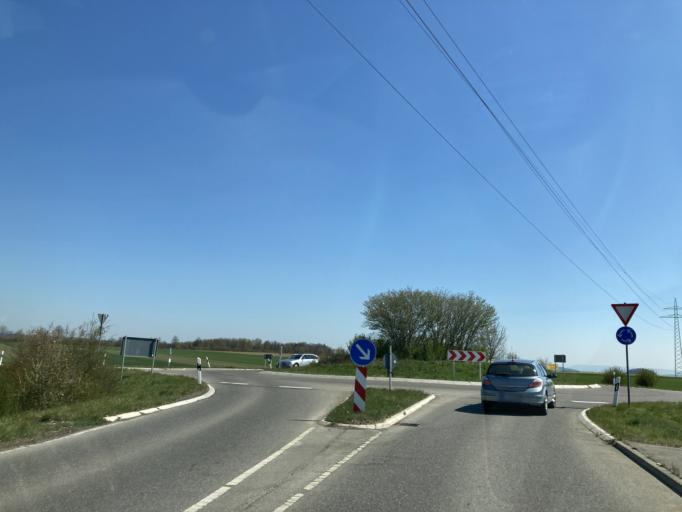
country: DE
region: Baden-Wuerttemberg
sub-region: Regierungsbezirk Stuttgart
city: Bondorf
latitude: 48.4983
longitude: 8.8441
